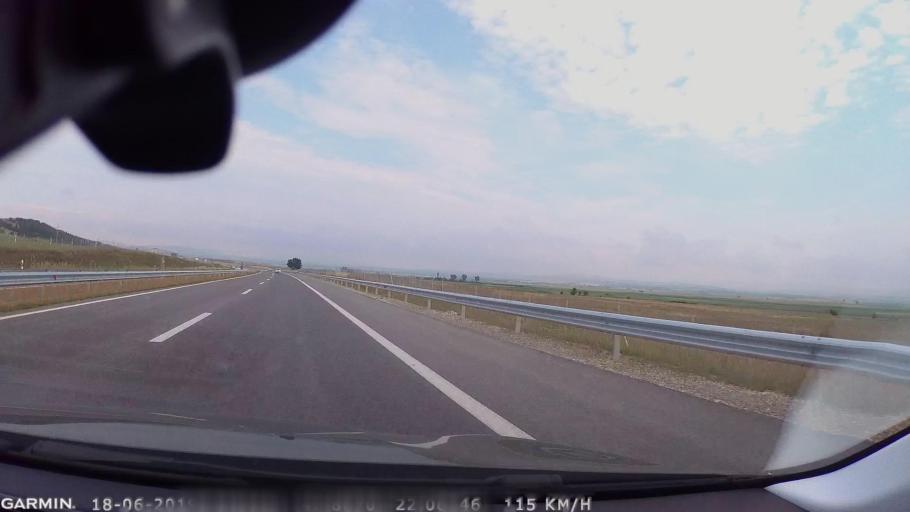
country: MK
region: Sveti Nikole
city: Sveti Nikole
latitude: 41.8073
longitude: 22.0637
